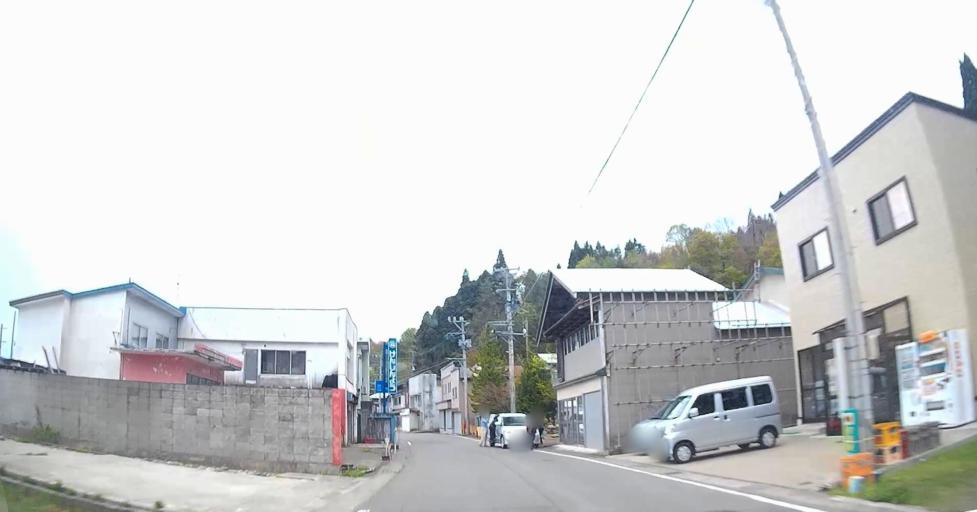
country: JP
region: Aomori
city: Shimokizukuri
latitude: 41.1971
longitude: 140.4300
